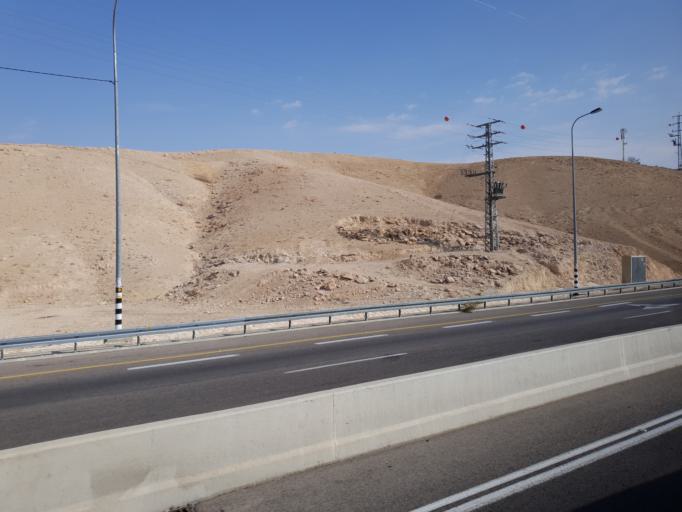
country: PS
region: West Bank
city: Jericho
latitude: 31.8154
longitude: 35.3635
